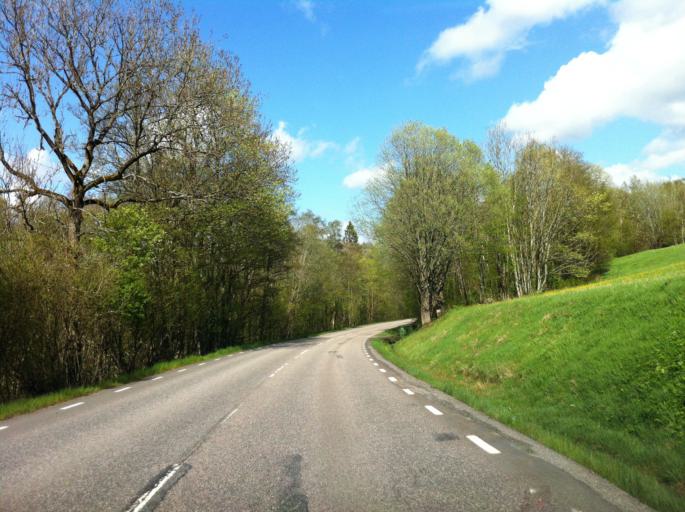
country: SE
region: Vaestra Goetaland
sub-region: Alingsas Kommun
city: Alingsas
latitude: 57.8623
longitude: 12.5652
